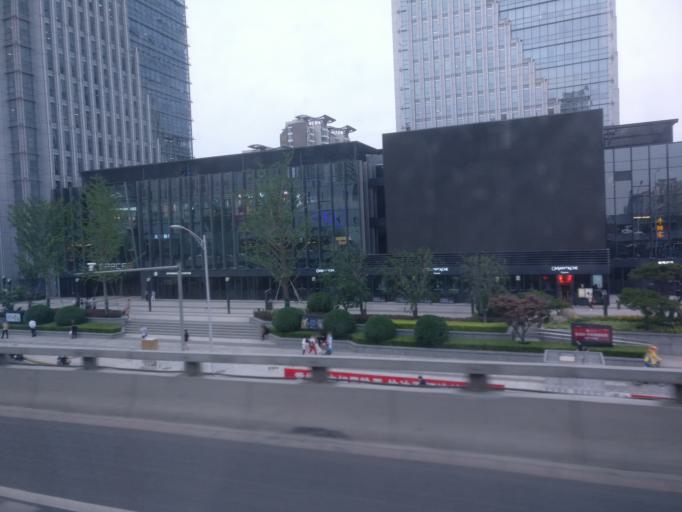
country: CN
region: Beijing
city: Longtan
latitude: 39.8926
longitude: 116.4554
